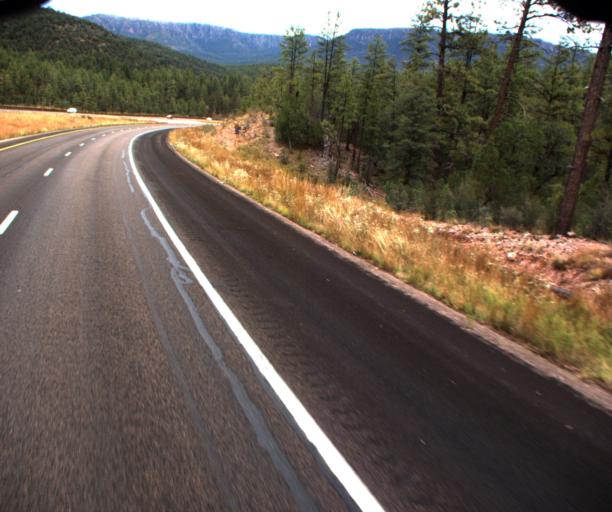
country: US
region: Arizona
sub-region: Gila County
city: Star Valley
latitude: 34.3208
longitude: -111.1139
